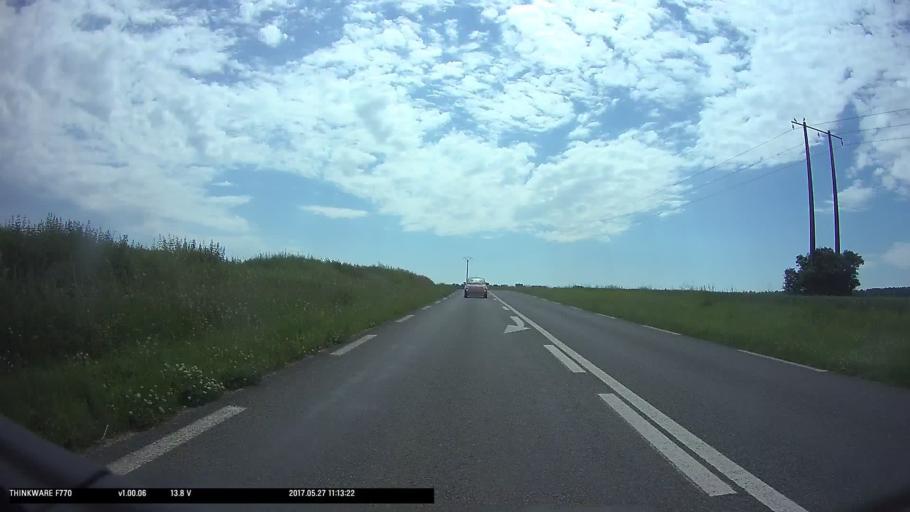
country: FR
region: Picardie
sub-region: Departement de l'Oise
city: Chaumont-en-Vexin
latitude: 49.2773
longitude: 1.8570
